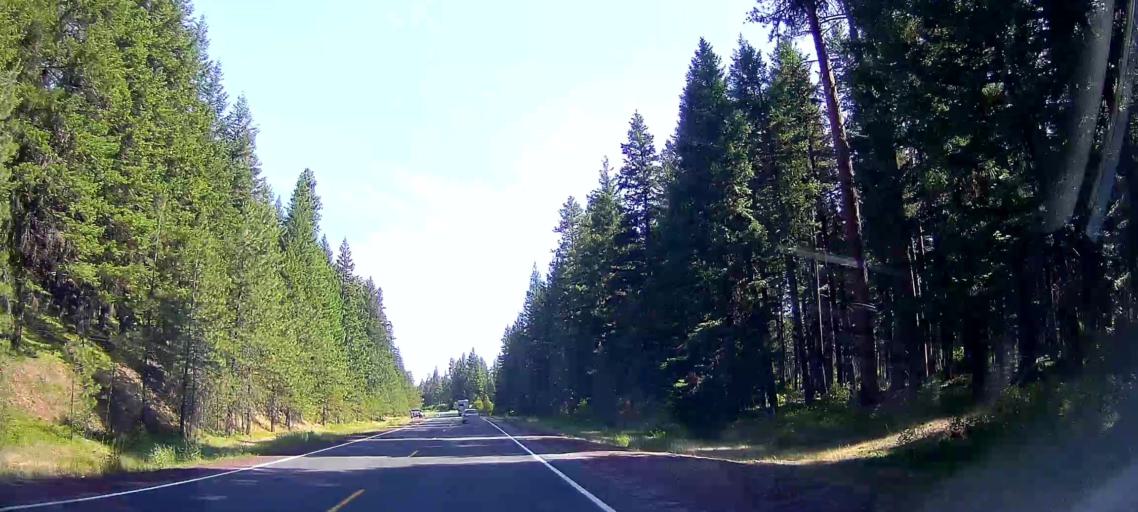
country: US
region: Oregon
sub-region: Jefferson County
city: Warm Springs
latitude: 45.0344
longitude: -121.5110
